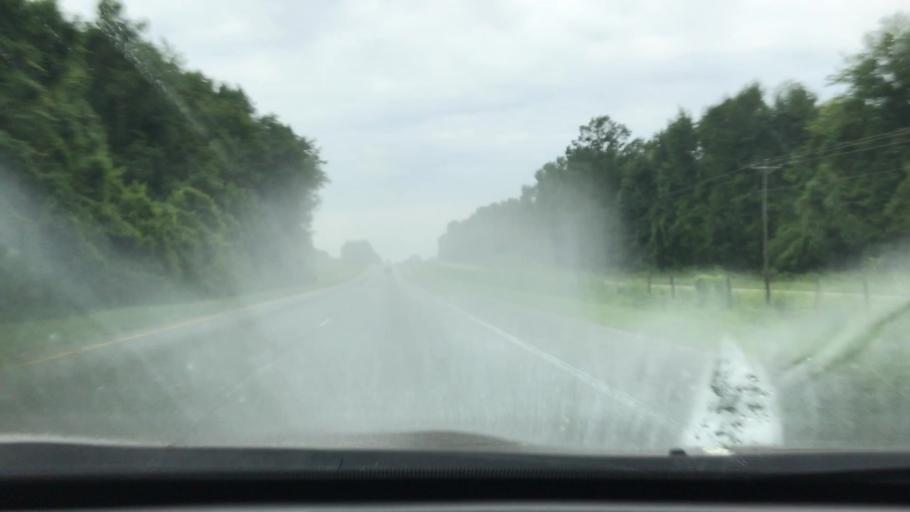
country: US
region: South Carolina
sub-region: Jasper County
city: Ridgeland
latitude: 32.5334
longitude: -80.9570
